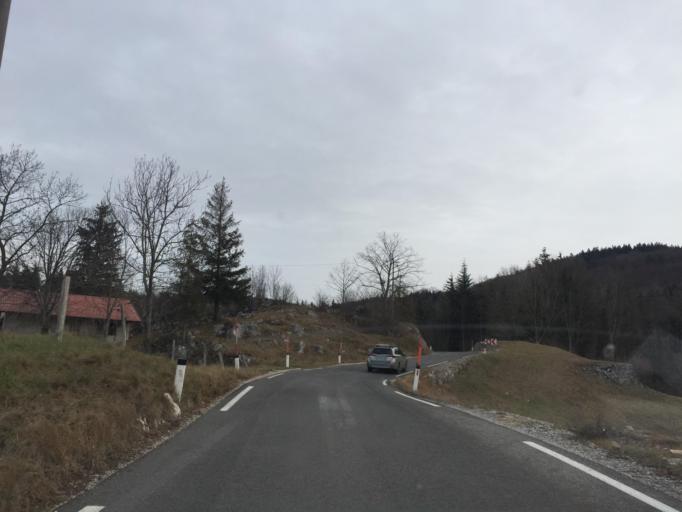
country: SI
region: Nova Gorica
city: Sempas
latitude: 45.9908
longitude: 13.7713
